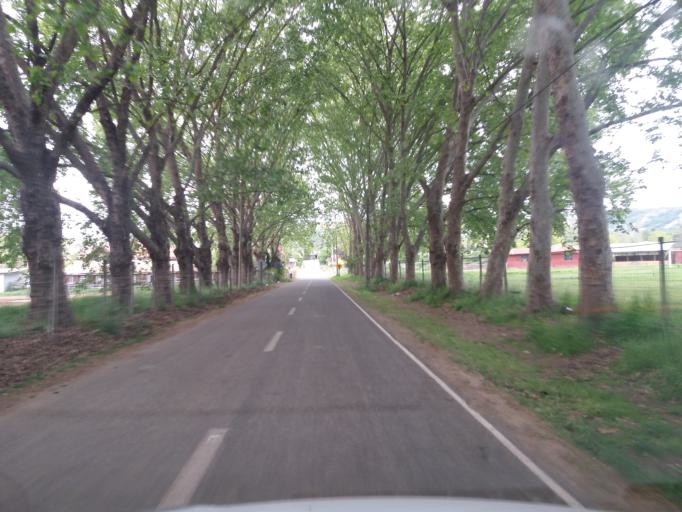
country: CL
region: Valparaiso
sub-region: Provincia de Quillota
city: Quillota
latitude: -32.8917
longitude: -71.3178
